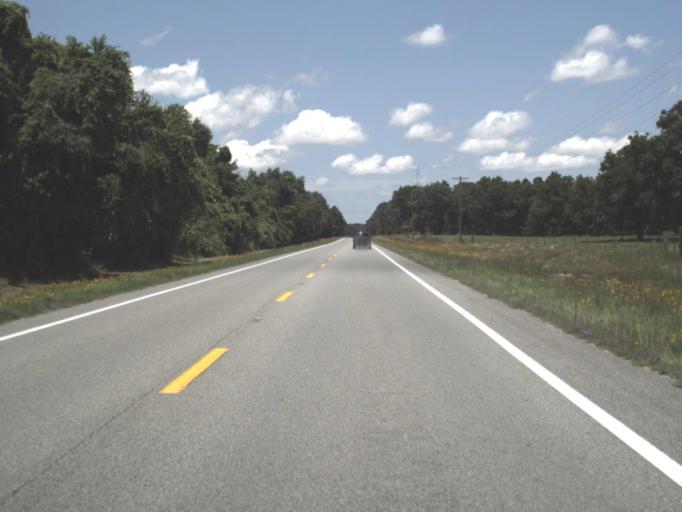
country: US
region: Florida
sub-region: Alachua County
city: High Springs
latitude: 29.9502
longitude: -82.7640
